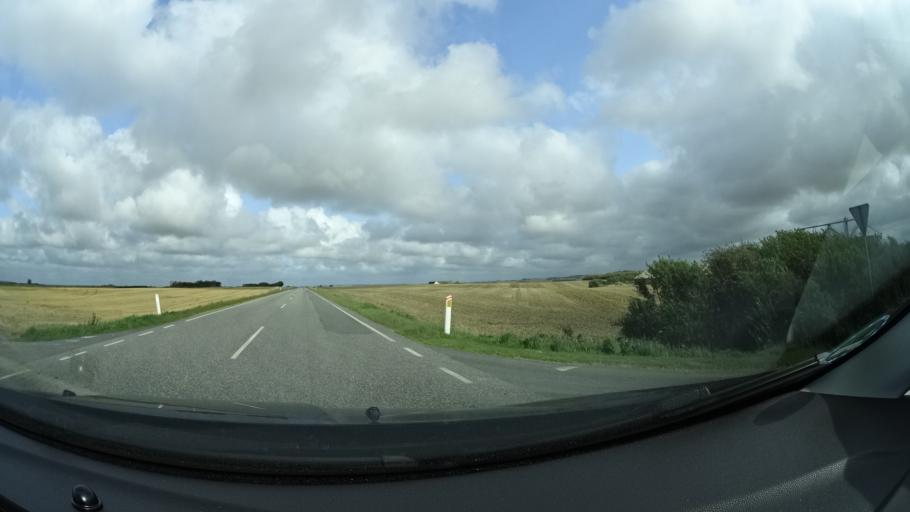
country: DK
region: Central Jutland
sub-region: Lemvig Kommune
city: Harboore
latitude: 56.5532
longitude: 8.1902
